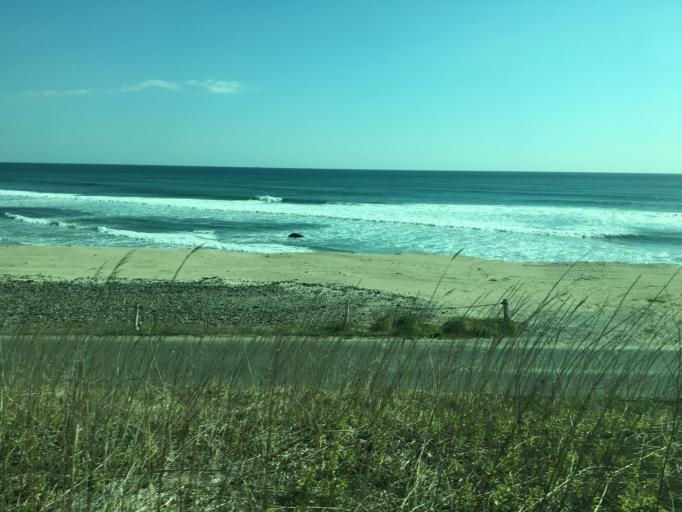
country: JP
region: Aomori
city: Hachinohe
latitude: 40.3214
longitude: 141.7737
